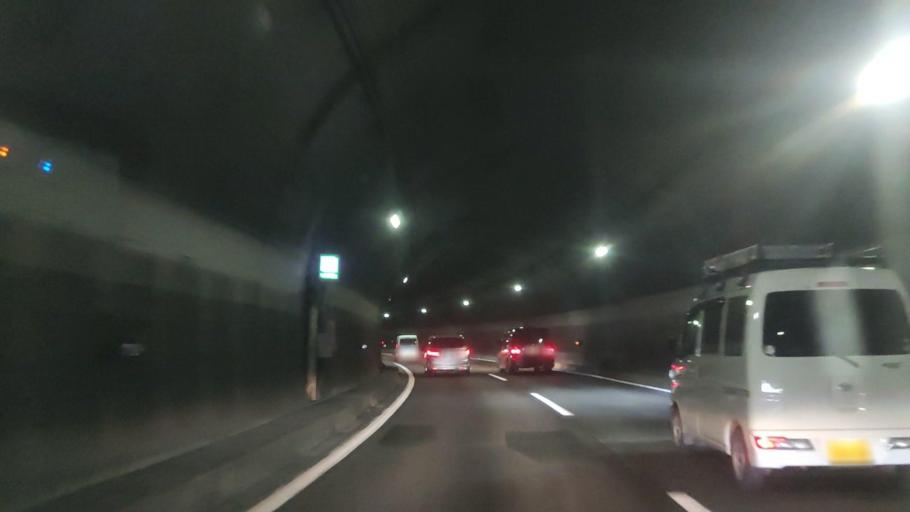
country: JP
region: Nagasaki
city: Obita
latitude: 32.8143
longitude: 129.9279
